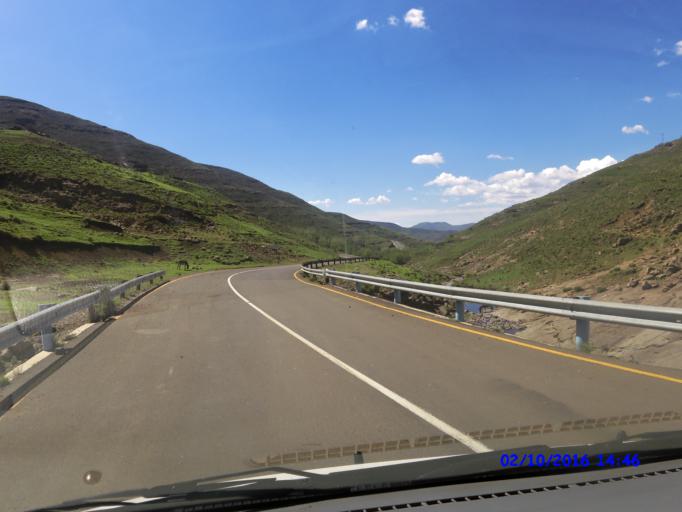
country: LS
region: Maseru
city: Nako
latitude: -29.5100
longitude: 28.0634
